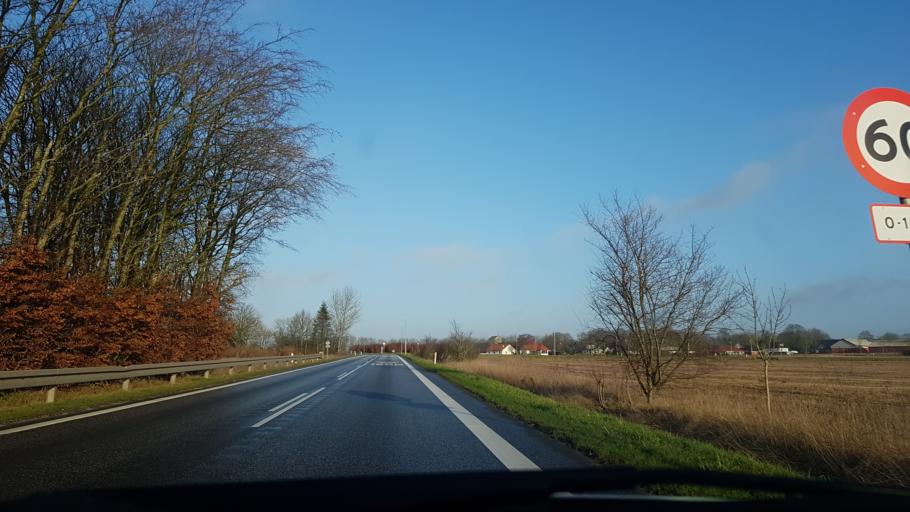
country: DK
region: South Denmark
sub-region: Tonder Kommune
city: Toftlund
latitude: 55.2522
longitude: 9.1438
